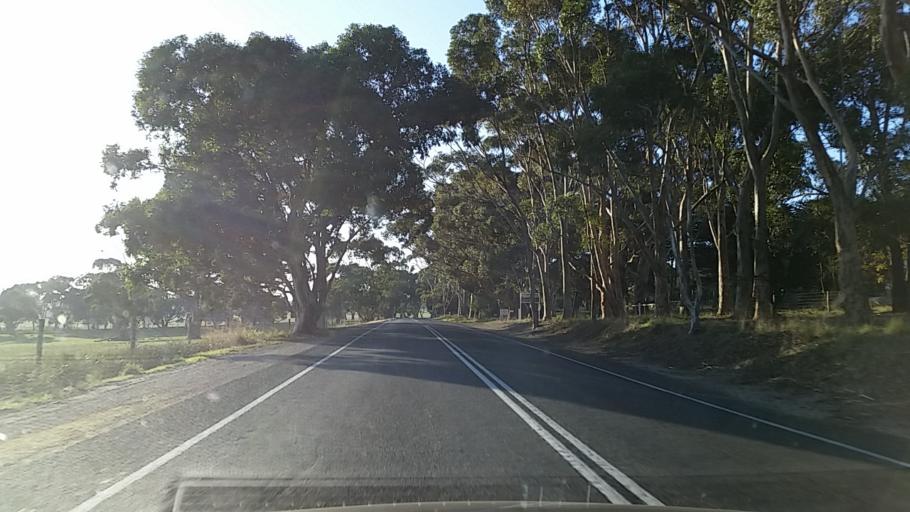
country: AU
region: South Australia
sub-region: Alexandrina
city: Goolwa
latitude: -35.3813
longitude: 138.7458
